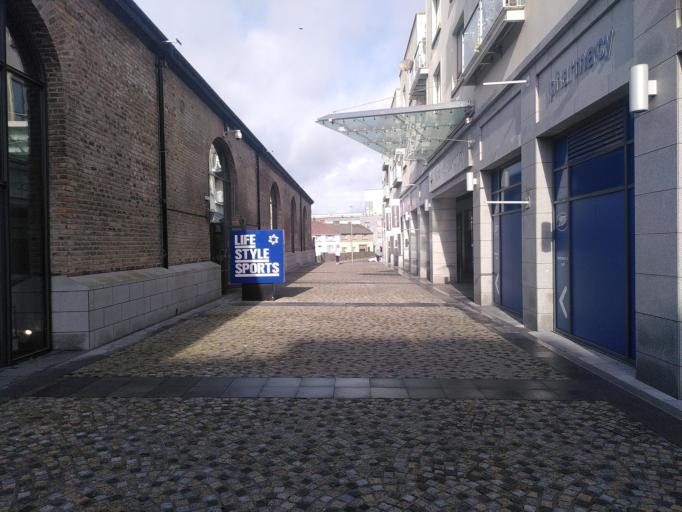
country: IE
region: Leinster
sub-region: Kilkenny
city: Kilkenny
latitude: 52.6554
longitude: -7.2441
